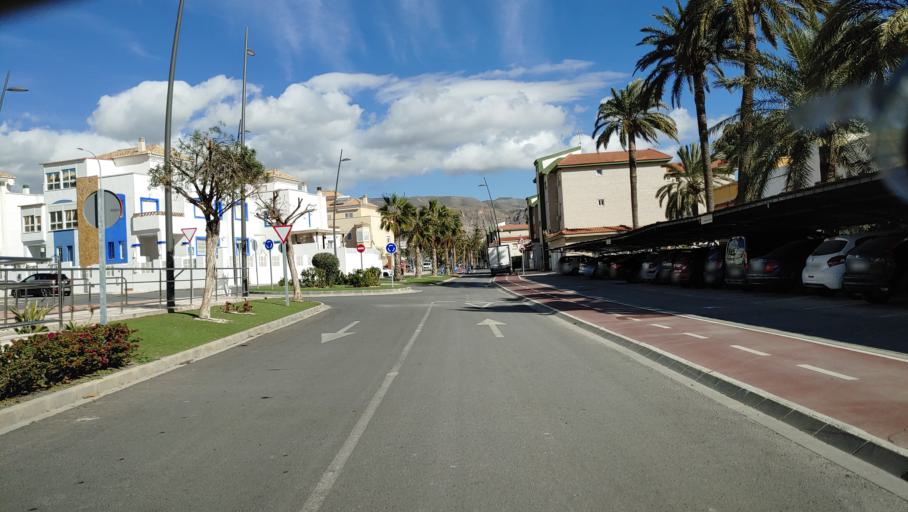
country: ES
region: Andalusia
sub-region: Provincia de Almeria
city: Aguadulce
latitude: 36.7961
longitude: -2.5839
